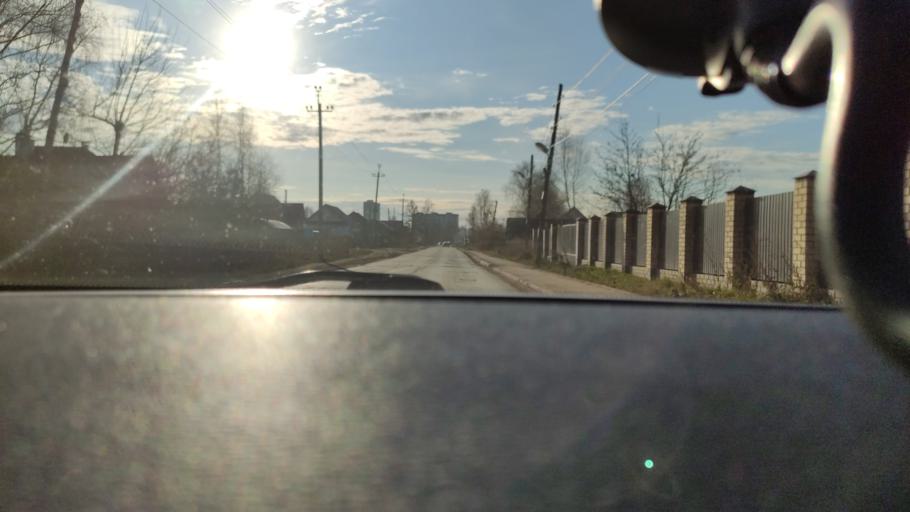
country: RU
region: Perm
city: Kondratovo
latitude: 58.0496
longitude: 56.0301
